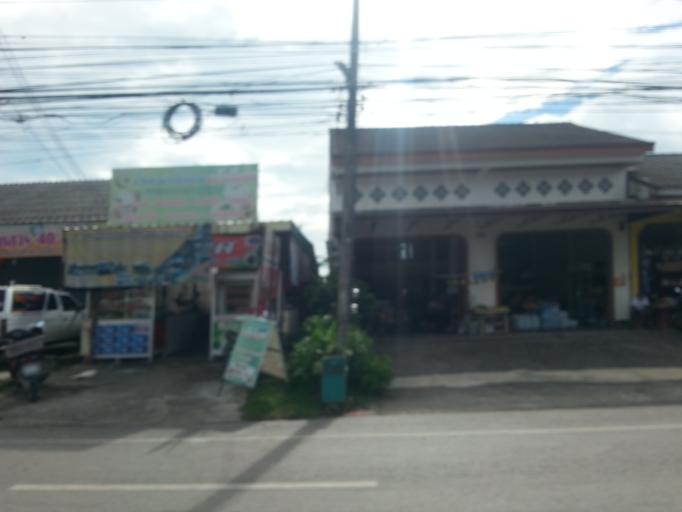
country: TH
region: Krabi
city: Nuea Khlong
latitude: 8.0664
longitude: 99.0020
